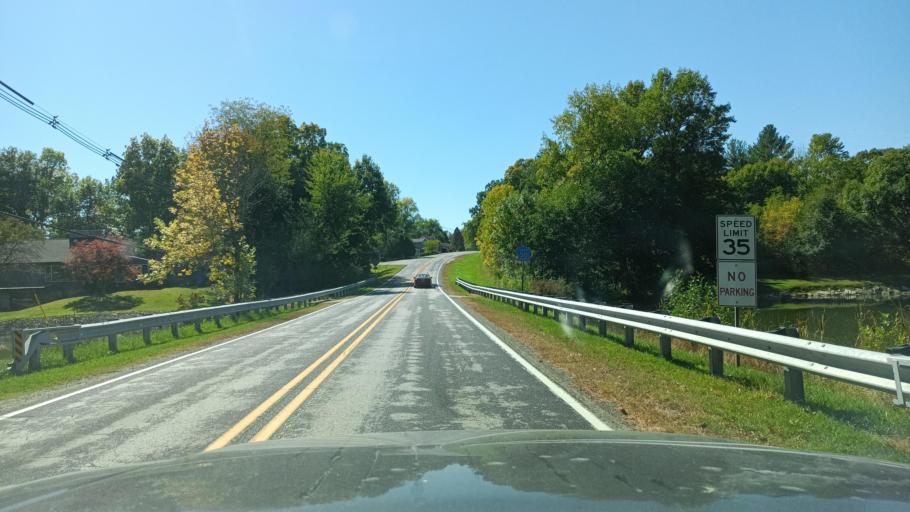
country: US
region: Illinois
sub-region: Champaign County
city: Lake of the Woods
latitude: 40.1977
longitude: -88.3783
